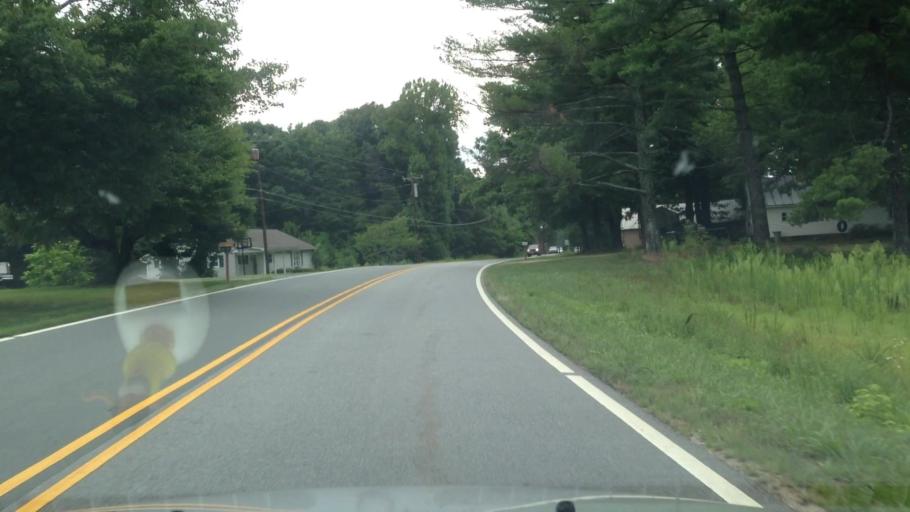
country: US
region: North Carolina
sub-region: Forsyth County
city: Kernersville
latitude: 36.1473
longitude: -80.0877
